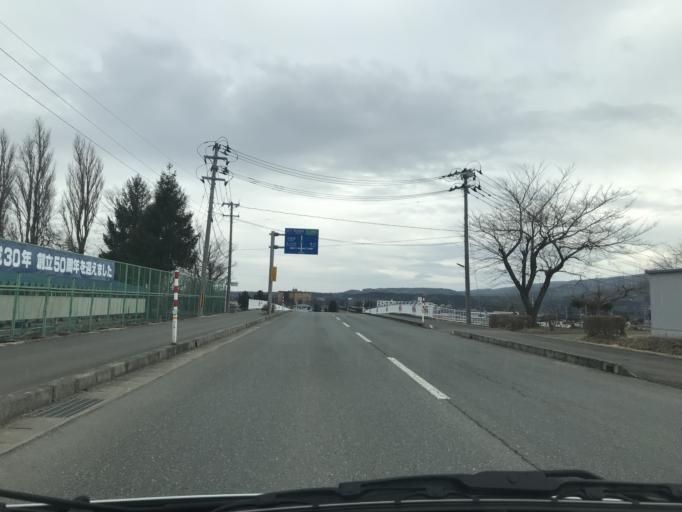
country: JP
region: Iwate
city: Kitakami
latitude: 39.3116
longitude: 140.9765
